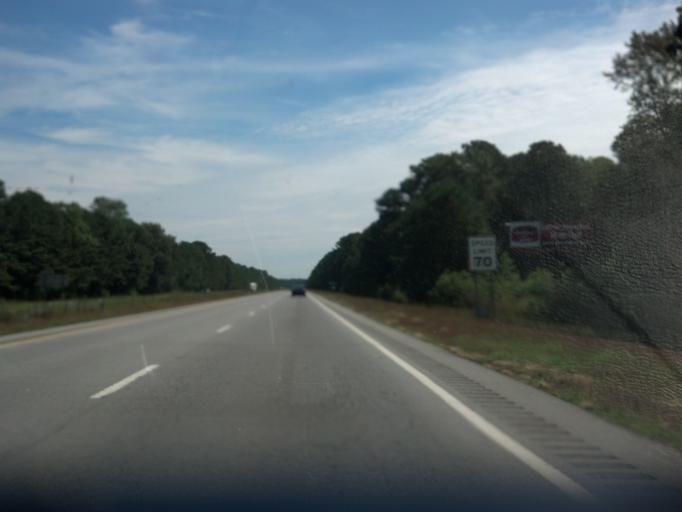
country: US
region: North Carolina
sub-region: Pitt County
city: Summerfield
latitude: 35.6082
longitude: -77.4704
